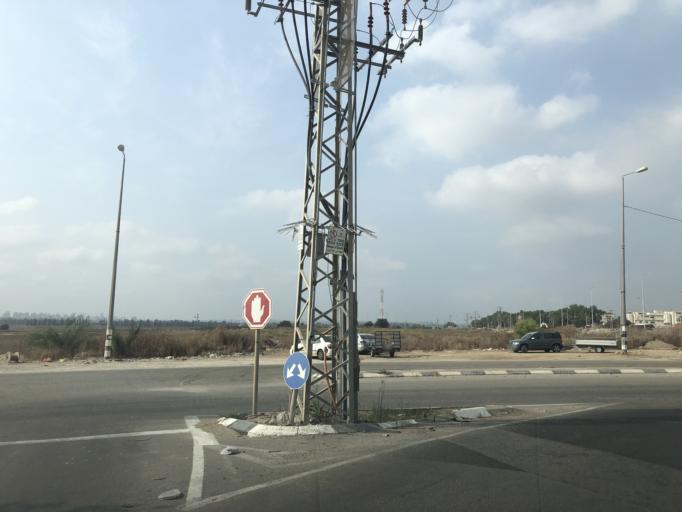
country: IL
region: Central District
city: Rosh Ha'Ayin
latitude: 32.0894
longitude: 34.9432
